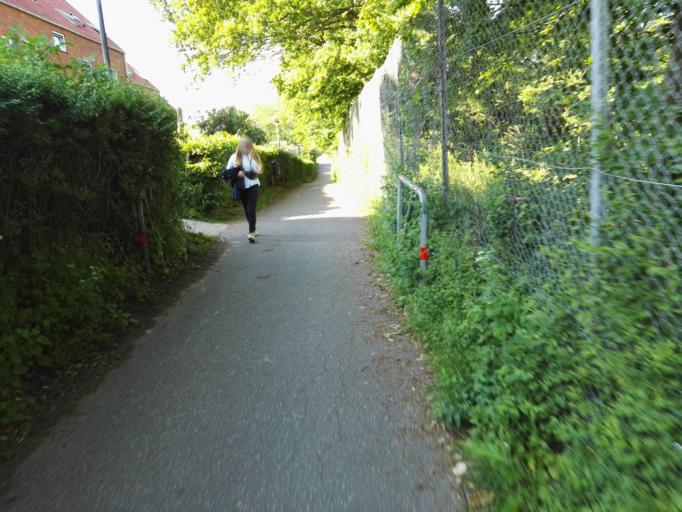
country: DK
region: Capital Region
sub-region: Ballerup Kommune
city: Malov
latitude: 55.7497
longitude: 12.3205
